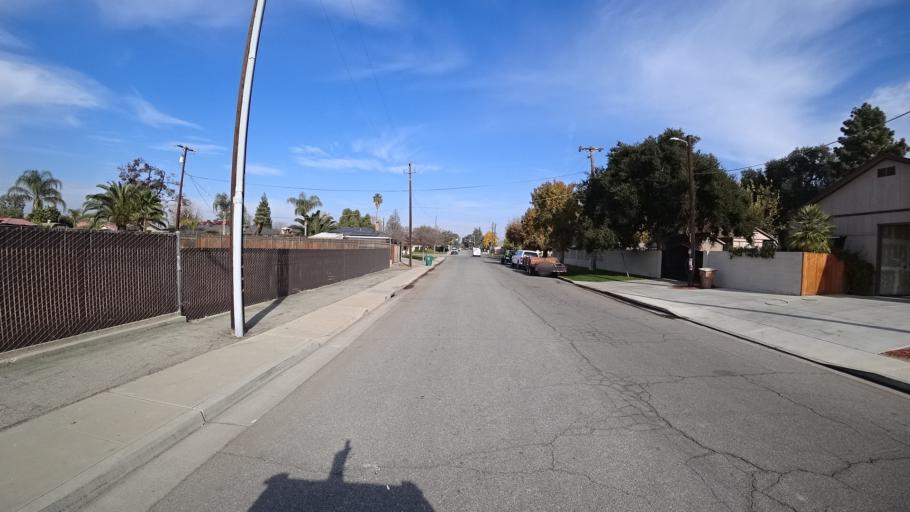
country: US
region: California
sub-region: Kern County
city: Greenacres
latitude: 35.4105
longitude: -119.0701
